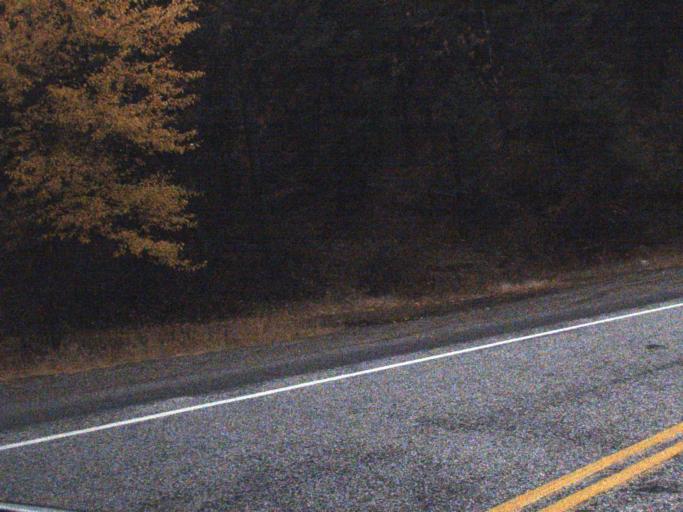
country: US
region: Washington
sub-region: Ferry County
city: Republic
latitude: 48.6123
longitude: -118.5663
